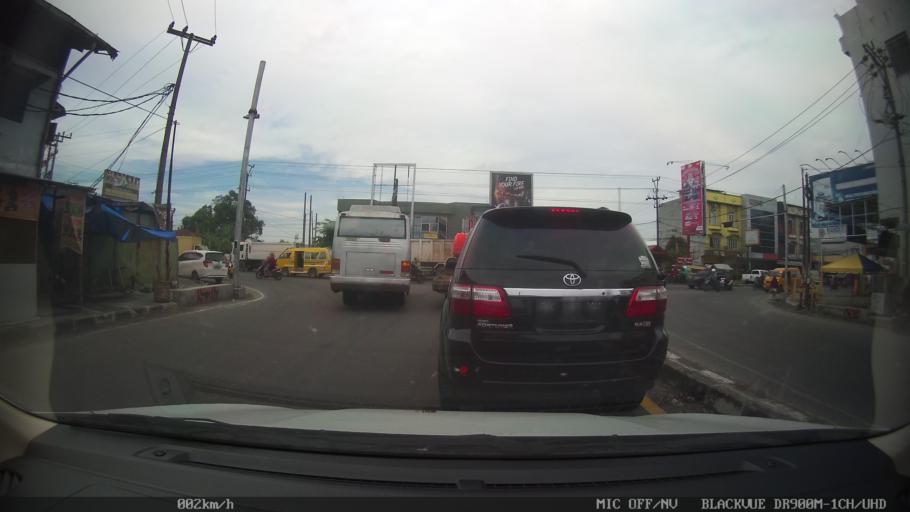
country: ID
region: North Sumatra
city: Sunggal
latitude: 3.5999
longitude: 98.5751
